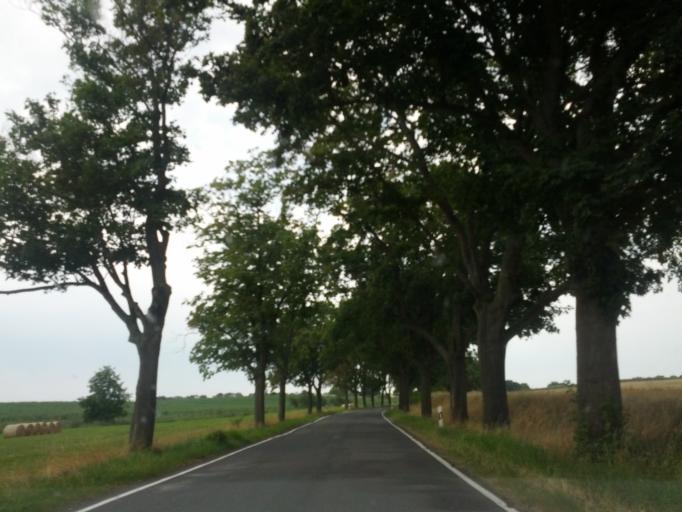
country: DE
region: Brandenburg
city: Kremmen
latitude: 52.7408
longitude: 12.9529
